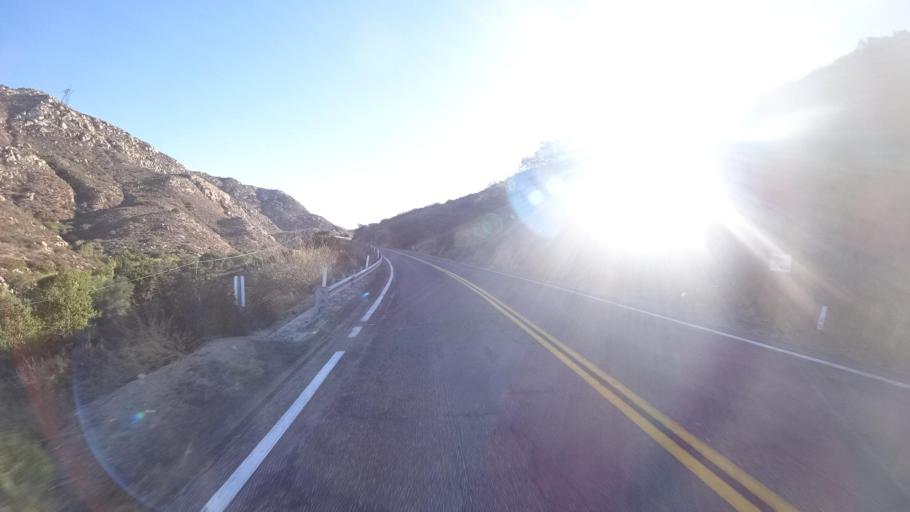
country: MX
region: Baja California
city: Tecate
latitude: 32.5968
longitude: -116.6574
